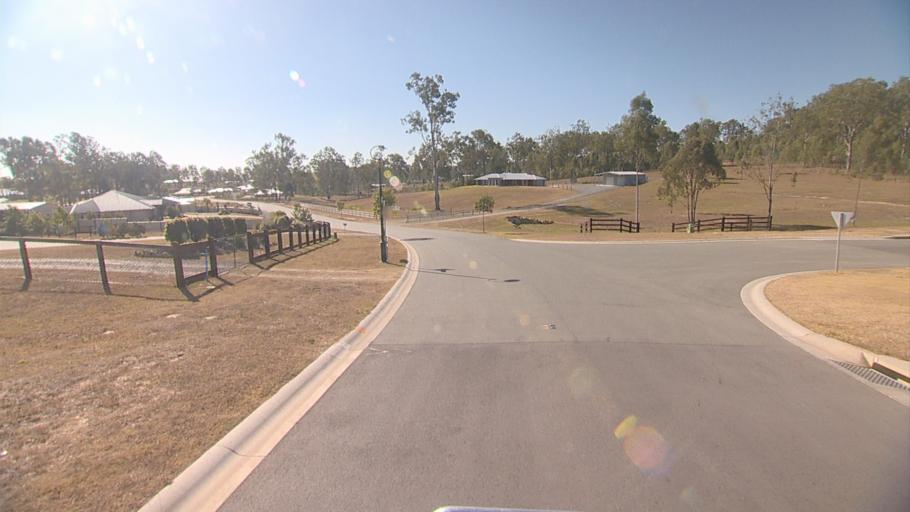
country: AU
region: Queensland
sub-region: Logan
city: Cedar Vale
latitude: -27.8721
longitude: 153.0564
